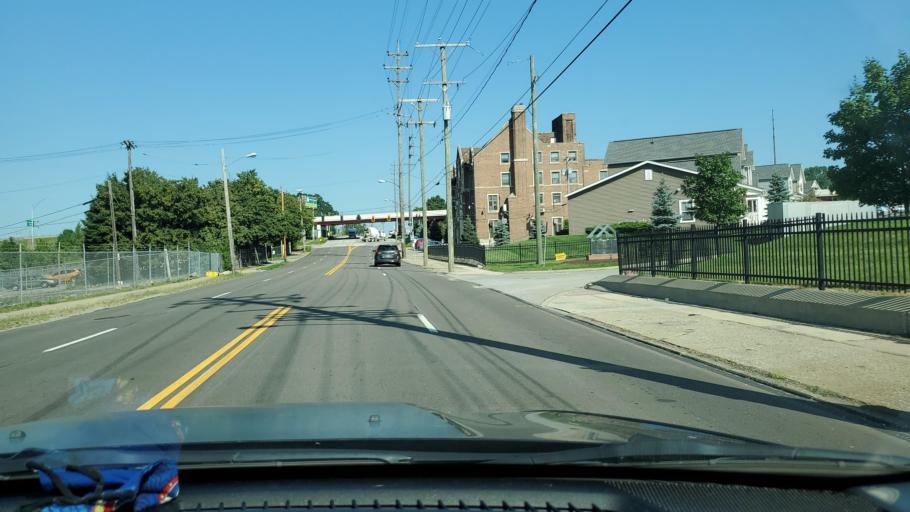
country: US
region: Ohio
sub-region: Mahoning County
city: Youngstown
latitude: 41.1100
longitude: -80.6641
